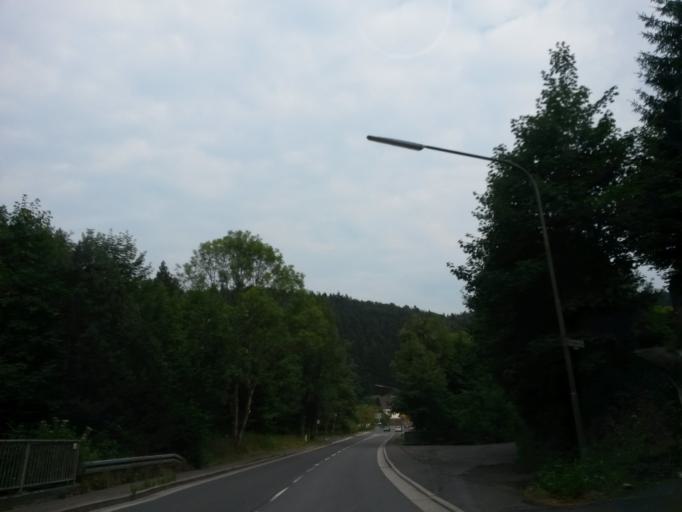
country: DE
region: North Rhine-Westphalia
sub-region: Regierungsbezirk Koln
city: Gummersbach
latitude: 51.0402
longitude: 7.5902
